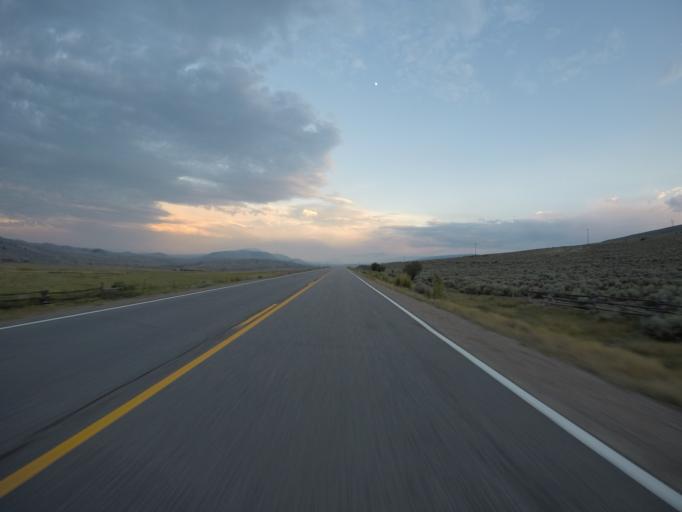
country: US
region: Colorado
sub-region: Grand County
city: Kremmling
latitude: 40.1047
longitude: -106.4242
